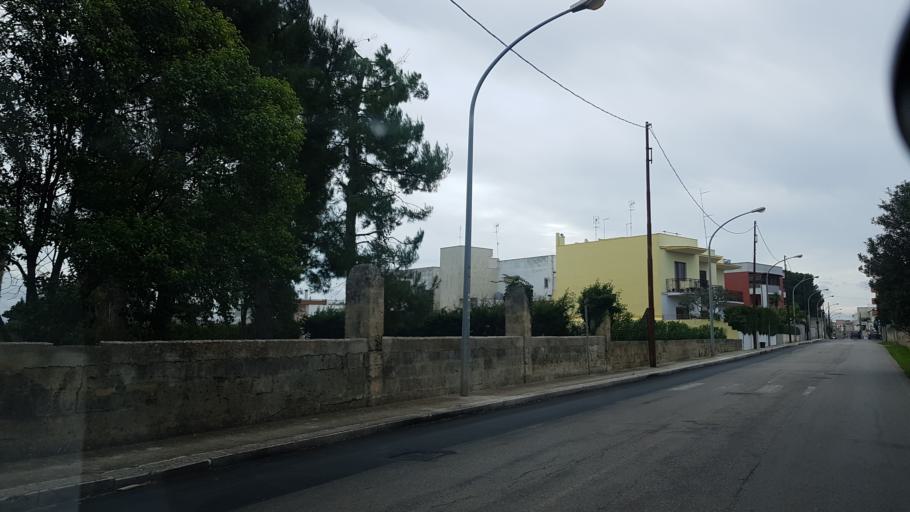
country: IT
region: Apulia
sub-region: Provincia di Brindisi
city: Mesagne
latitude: 40.5666
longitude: 17.8014
